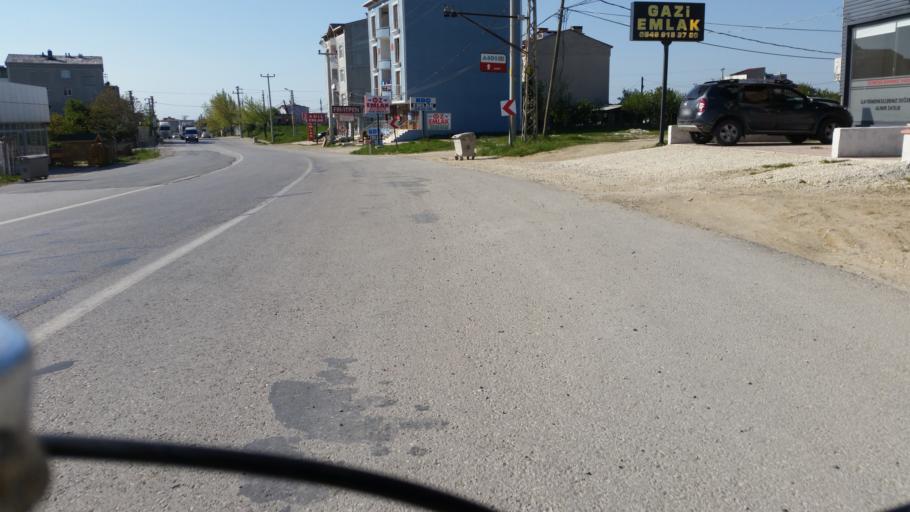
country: TR
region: Tekirdag
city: Cerkezkoey
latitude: 41.3559
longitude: 27.9542
